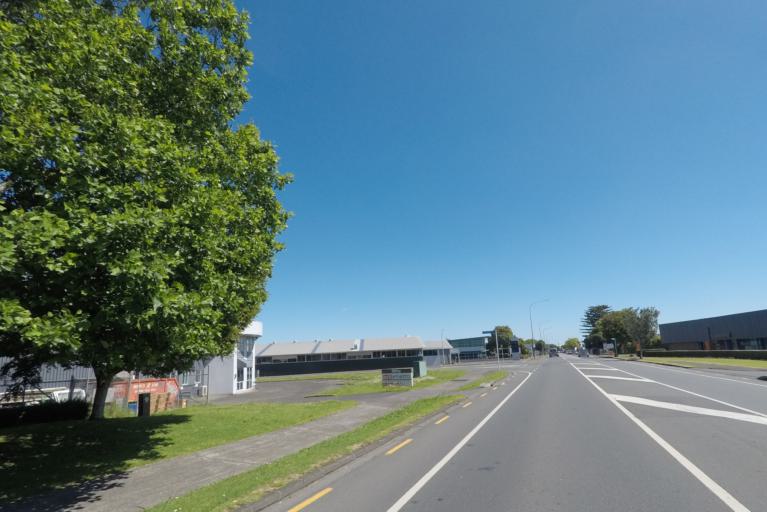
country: NZ
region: Auckland
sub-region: Auckland
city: Rosebank
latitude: -36.8765
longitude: 174.6699
